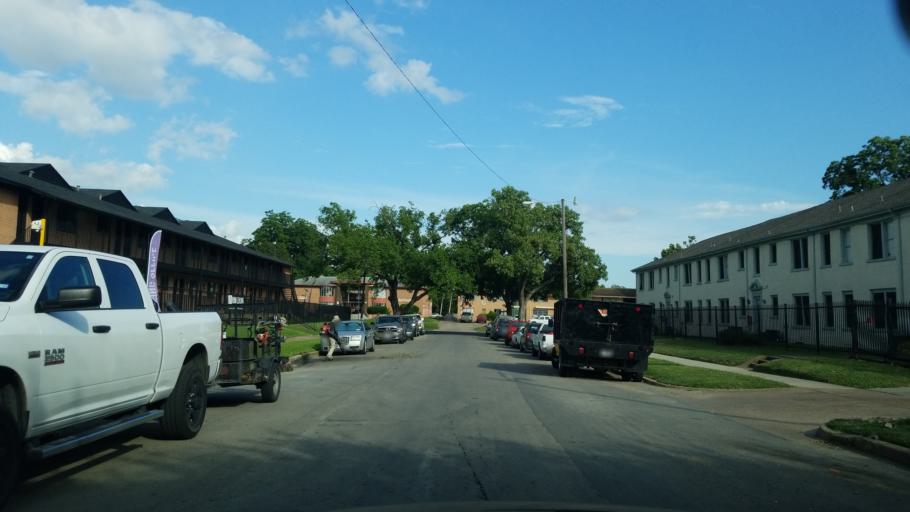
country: US
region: Texas
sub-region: Dallas County
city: Highland Park
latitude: 32.8053
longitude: -96.7708
